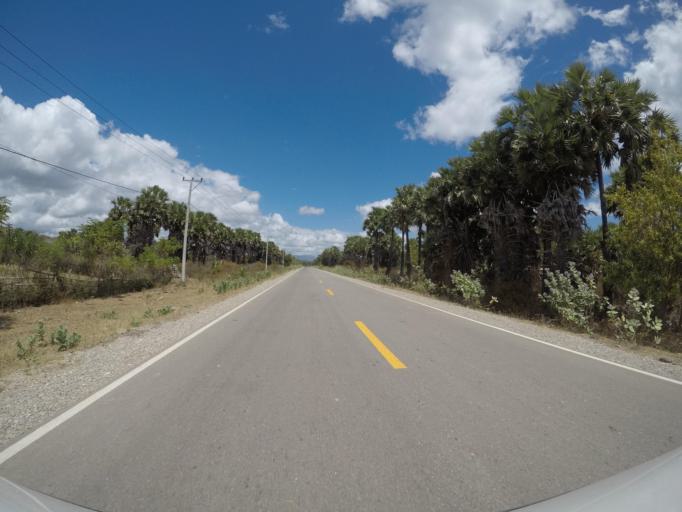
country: TL
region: Lautem
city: Lospalos
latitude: -8.3868
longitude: 126.8545
